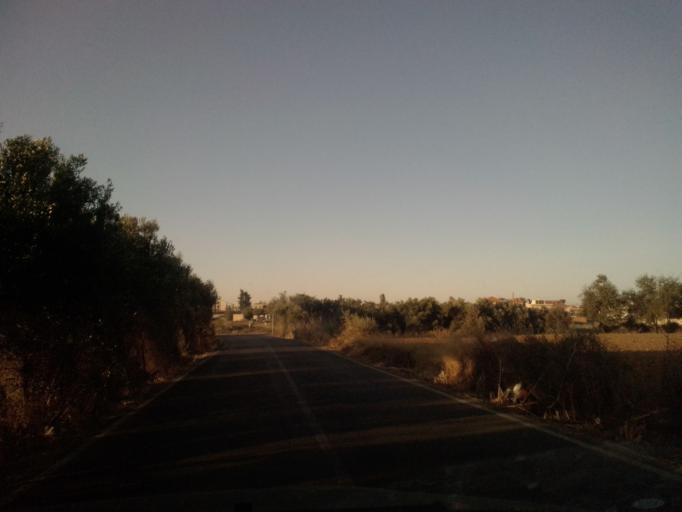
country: CY
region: Limassol
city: Ypsonas
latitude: 34.6632
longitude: 32.9626
